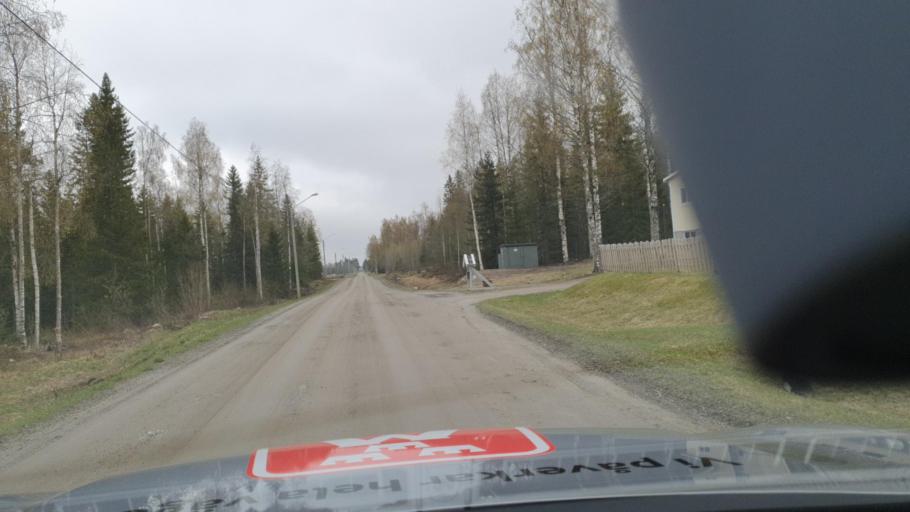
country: SE
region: Vaesterbotten
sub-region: Bjurholms Kommun
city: Bjurholm
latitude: 63.6556
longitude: 19.0369
